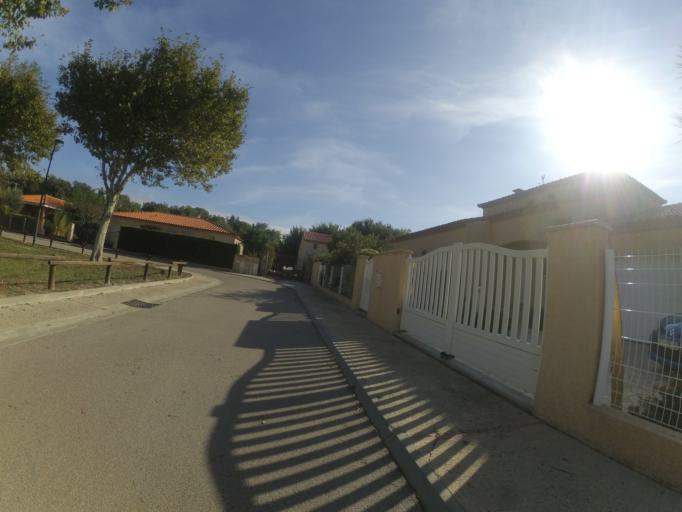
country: FR
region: Languedoc-Roussillon
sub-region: Departement des Pyrenees-Orientales
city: Pezilla-la-Riviere
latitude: 42.6915
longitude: 2.7644
